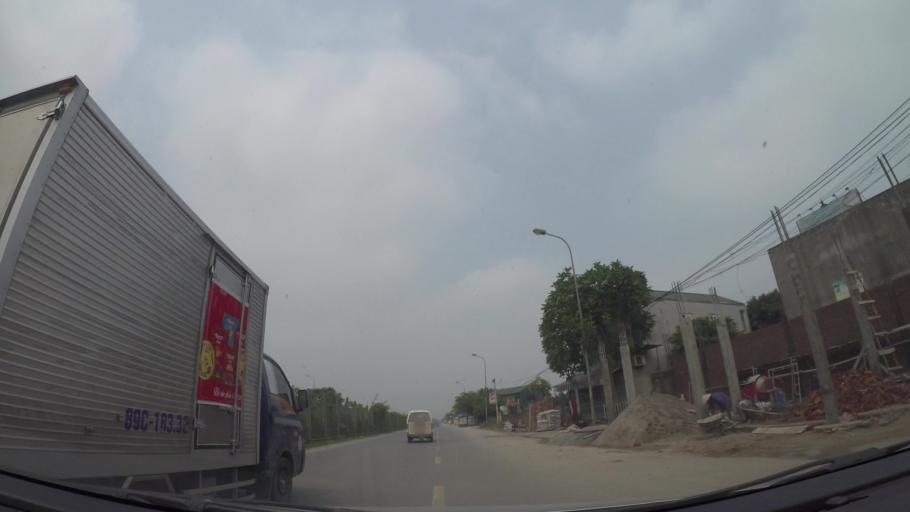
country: VN
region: Ha Noi
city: Quoc Oai
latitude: 21.0041
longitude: 105.6693
